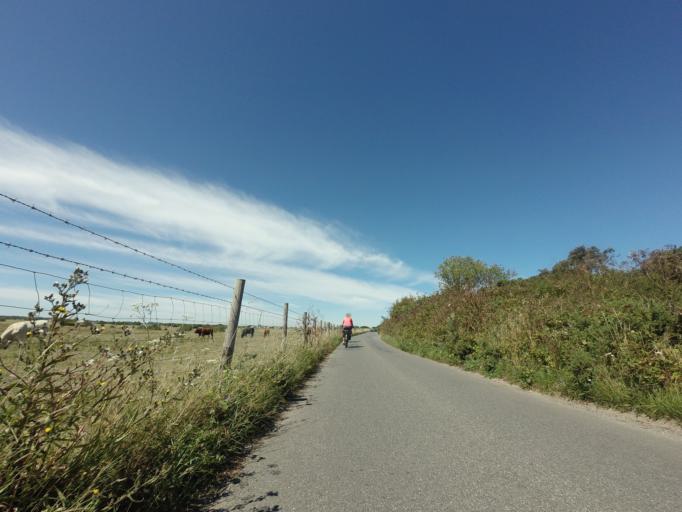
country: GB
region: England
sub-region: Kent
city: Deal
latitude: 51.2445
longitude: 1.3957
